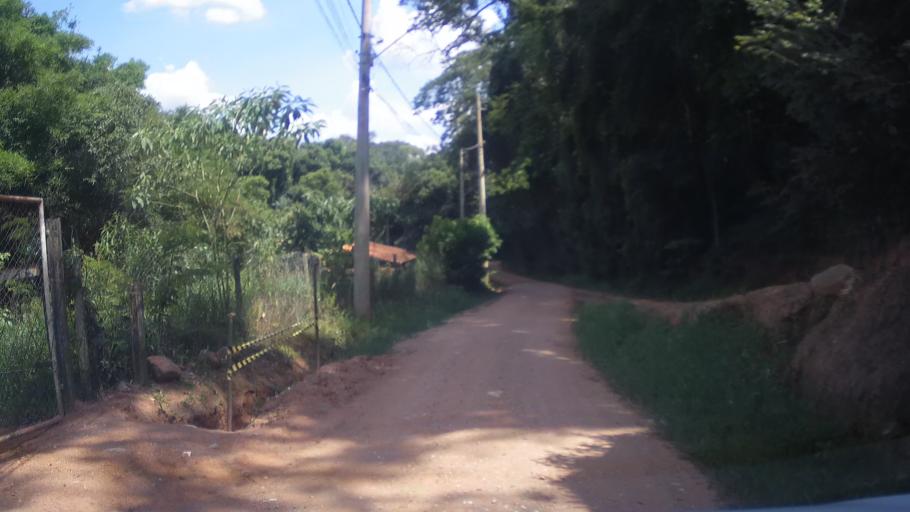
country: BR
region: Sao Paulo
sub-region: Jarinu
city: Jarinu
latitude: -23.1154
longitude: -46.8099
